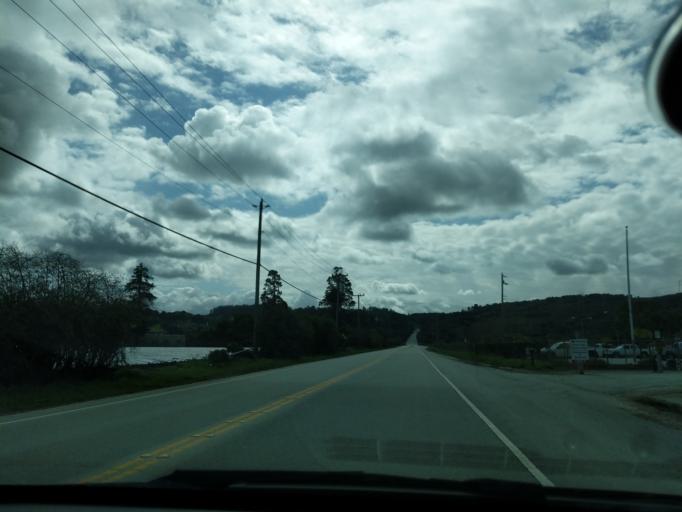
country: US
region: California
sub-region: San Benito County
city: Aromas
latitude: 36.8936
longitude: -121.6729
